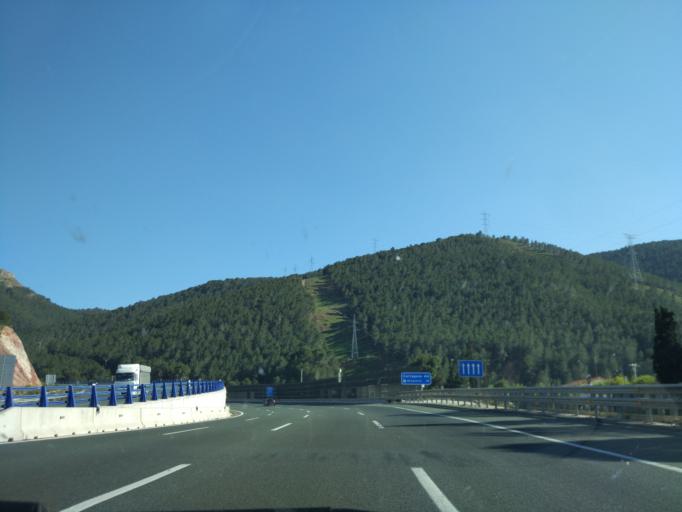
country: ES
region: Murcia
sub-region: Murcia
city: Alcantarilla
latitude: 37.9109
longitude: -1.1637
